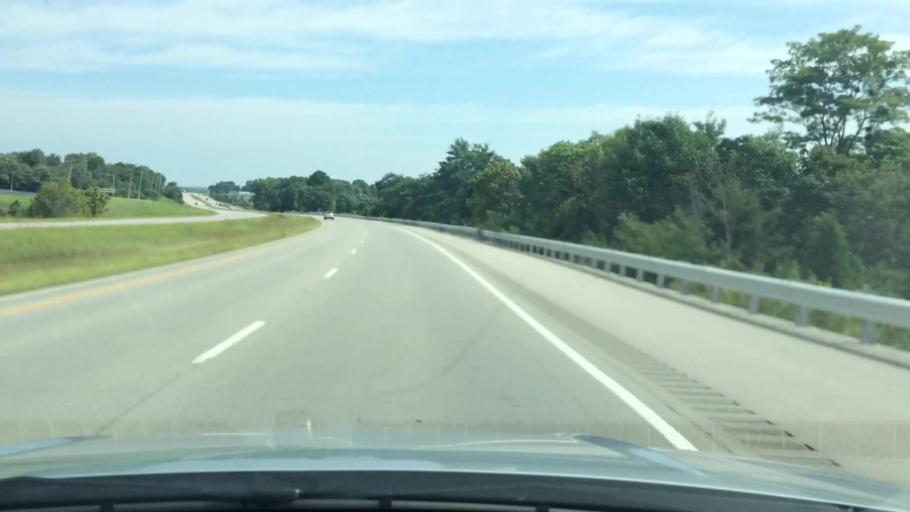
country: US
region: Kentucky
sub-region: Franklin County
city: Frankfort
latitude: 38.1378
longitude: -84.9050
